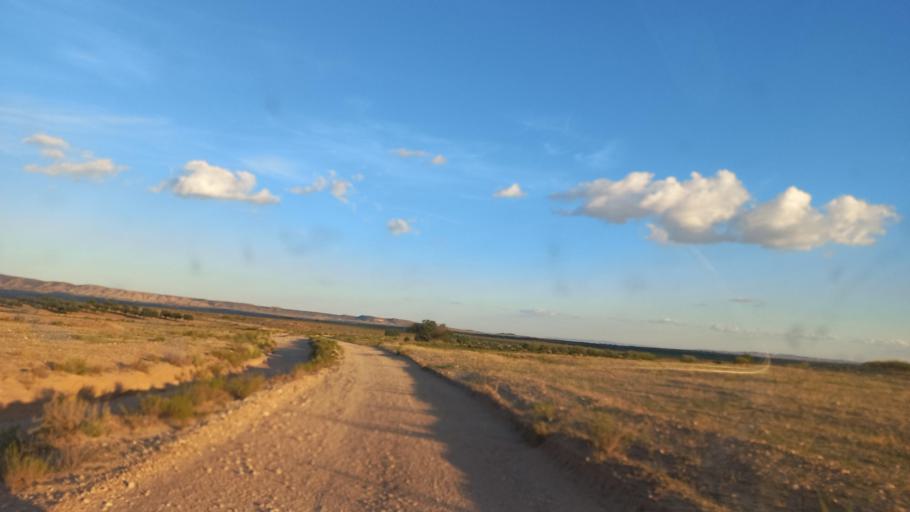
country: TN
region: Al Qasrayn
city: Sbiba
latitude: 35.3488
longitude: 9.0248
